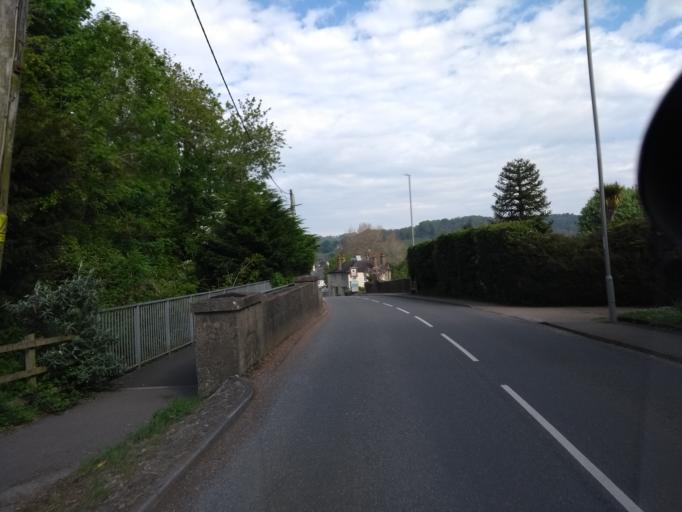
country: GB
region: England
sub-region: Dorset
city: Lyme Regis
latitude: 50.7318
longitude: -2.9486
